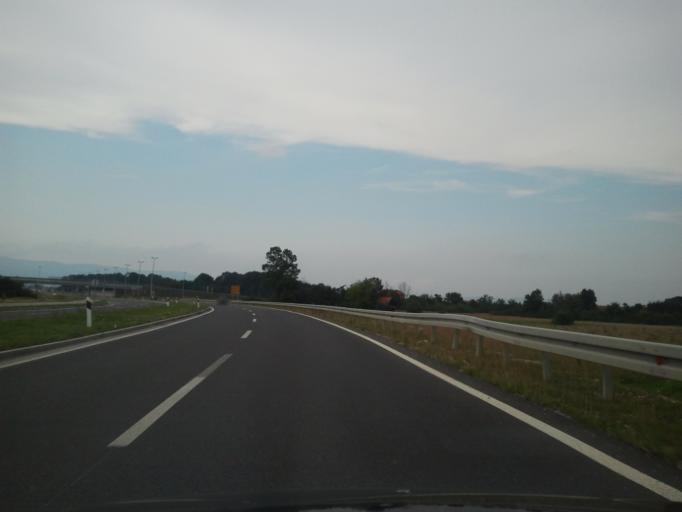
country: HR
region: Zagrebacka
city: Micevec
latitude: 45.7464
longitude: 16.1072
